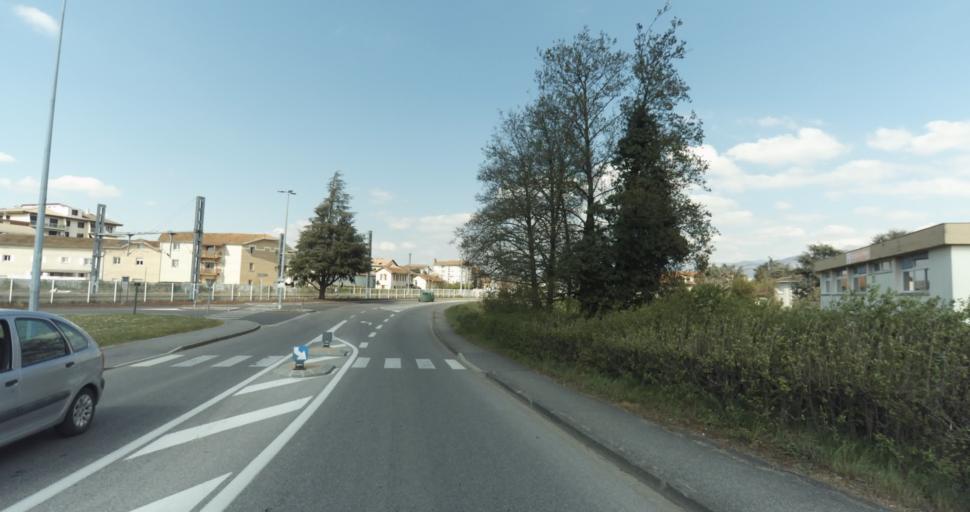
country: FR
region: Rhone-Alpes
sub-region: Departement de l'Isere
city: Saint-Marcellin
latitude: 45.1482
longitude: 5.3191
